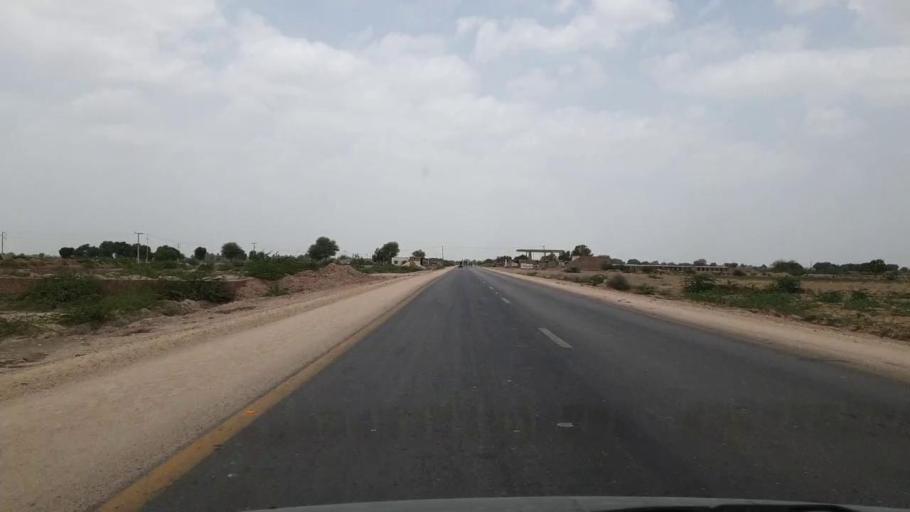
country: PK
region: Sindh
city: Naukot
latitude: 24.8428
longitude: 69.4422
